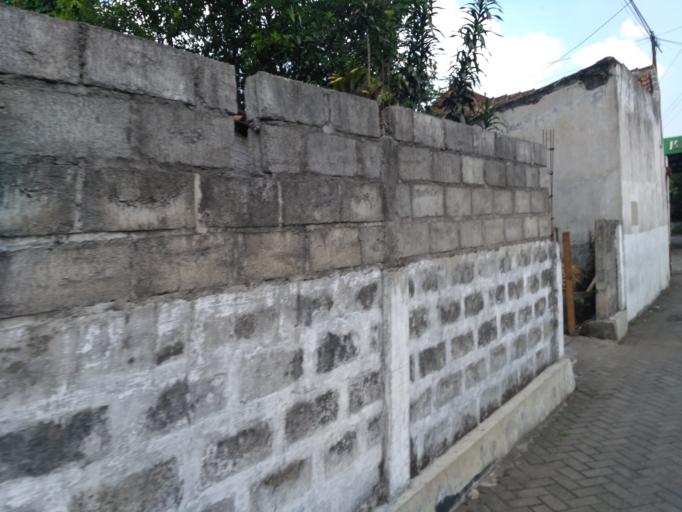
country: ID
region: Daerah Istimewa Yogyakarta
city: Melati
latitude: -7.7575
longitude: 110.3717
